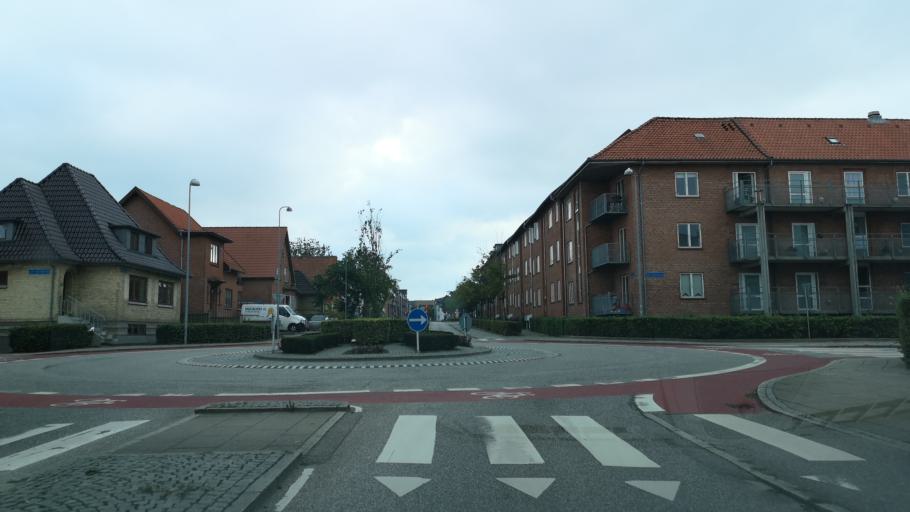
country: DK
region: Central Jutland
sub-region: Herning Kommune
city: Herning
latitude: 56.1401
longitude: 8.9796
